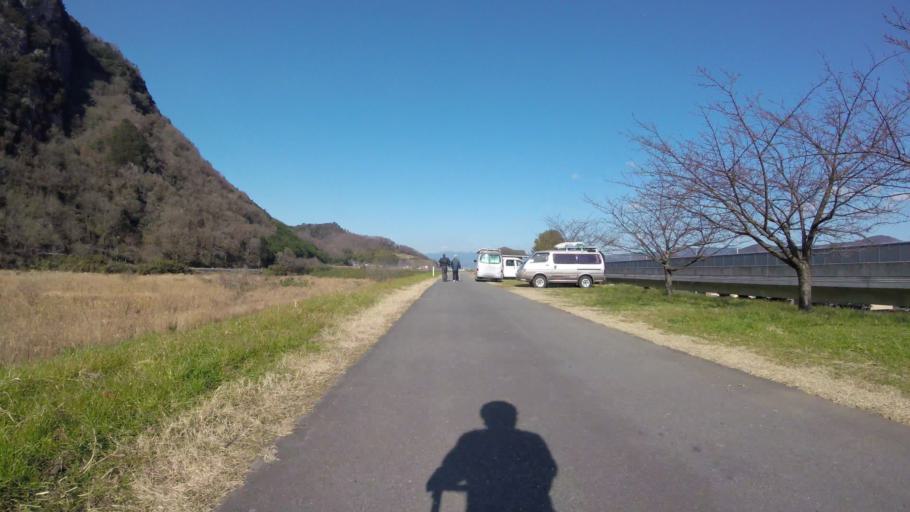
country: JP
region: Shizuoka
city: Mishima
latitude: 35.0013
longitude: 138.9352
